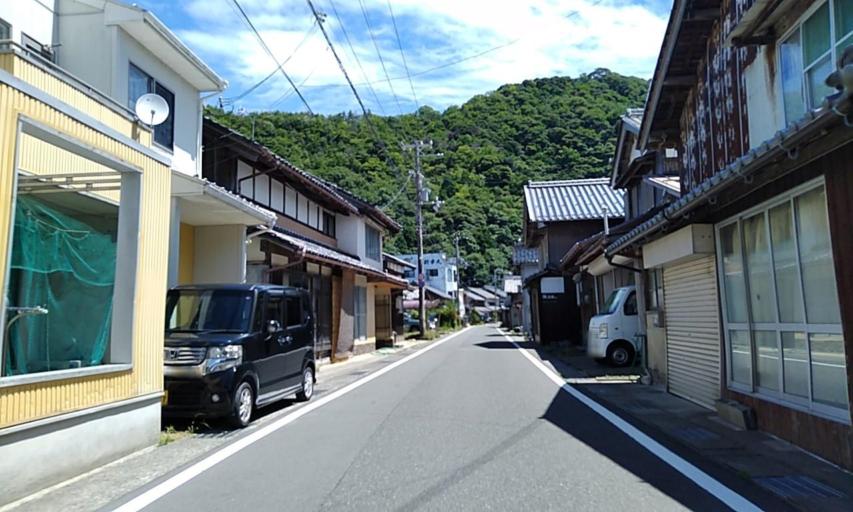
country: JP
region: Kyoto
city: Miyazu
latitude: 35.6674
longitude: 135.2680
